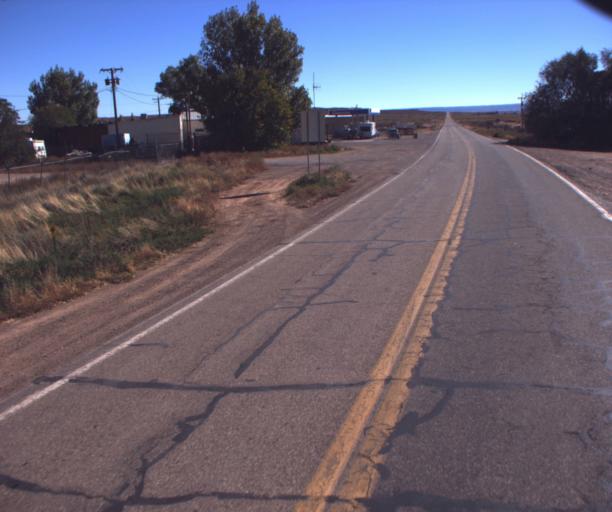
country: US
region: Arizona
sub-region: Coconino County
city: Fredonia
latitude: 36.9401
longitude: -112.5227
